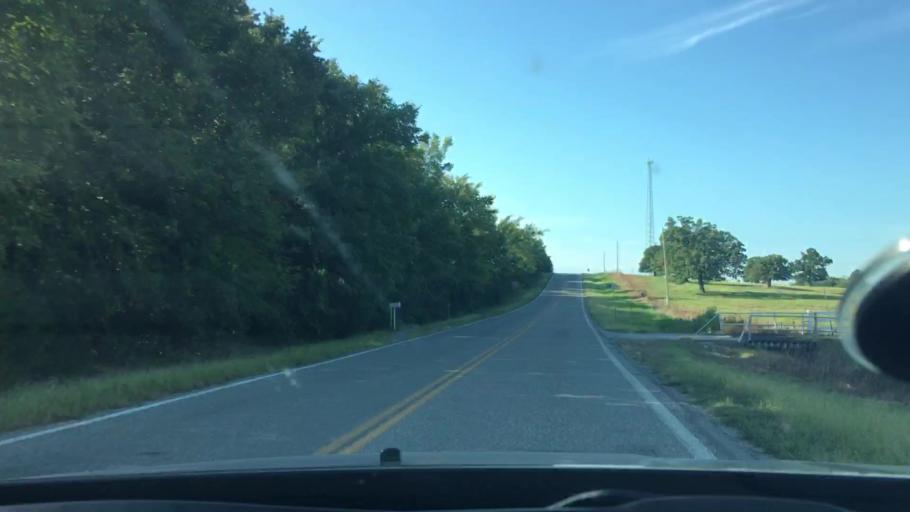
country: US
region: Oklahoma
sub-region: Coal County
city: Coalgate
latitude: 34.6181
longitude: -96.4243
